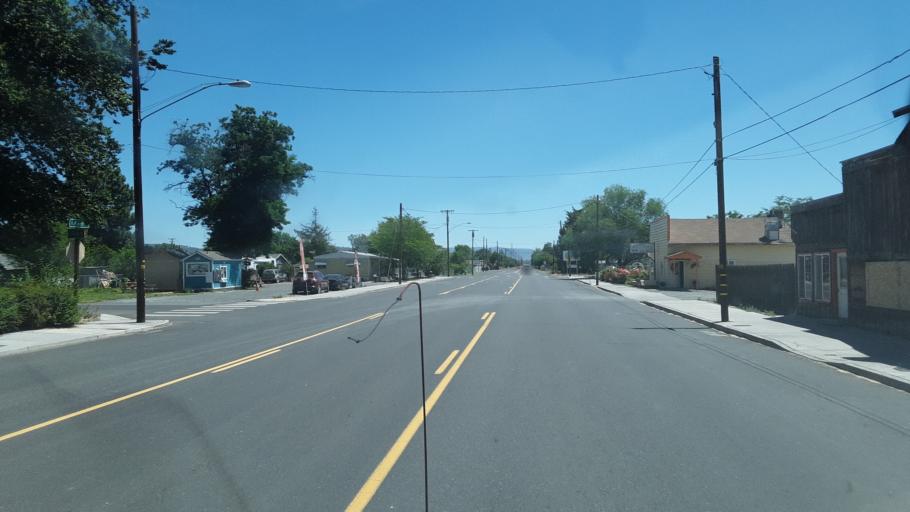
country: US
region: California
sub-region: Siskiyou County
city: Tulelake
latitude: 42.0239
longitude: -121.5971
